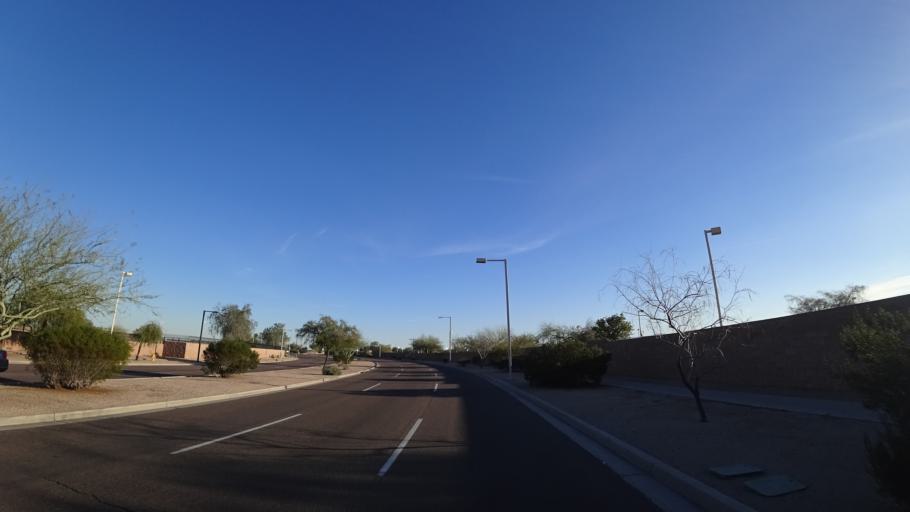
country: US
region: Arizona
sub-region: Maricopa County
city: Phoenix
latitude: 33.4306
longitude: -112.0346
